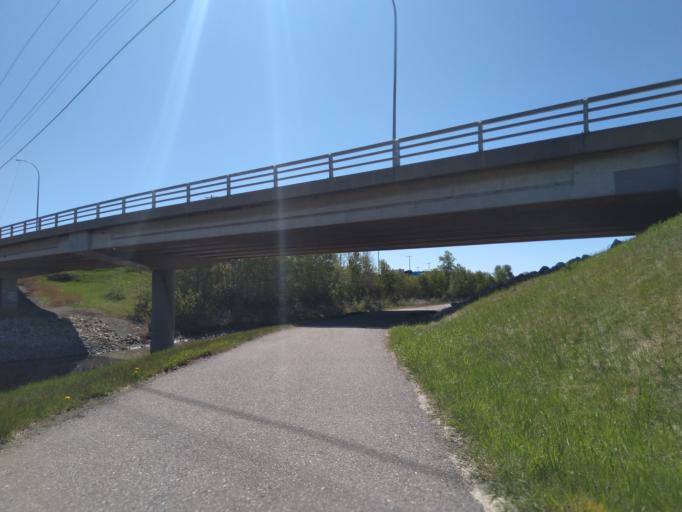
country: CA
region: Alberta
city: Calgary
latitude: 50.9989
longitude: -113.9928
